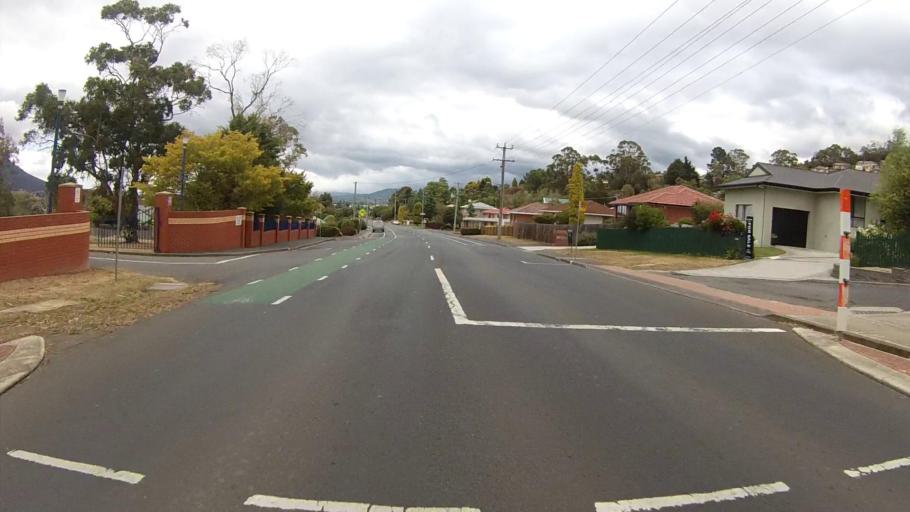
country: AU
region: Tasmania
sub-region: Glenorchy
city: Claremont
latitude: -42.7752
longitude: 147.2502
